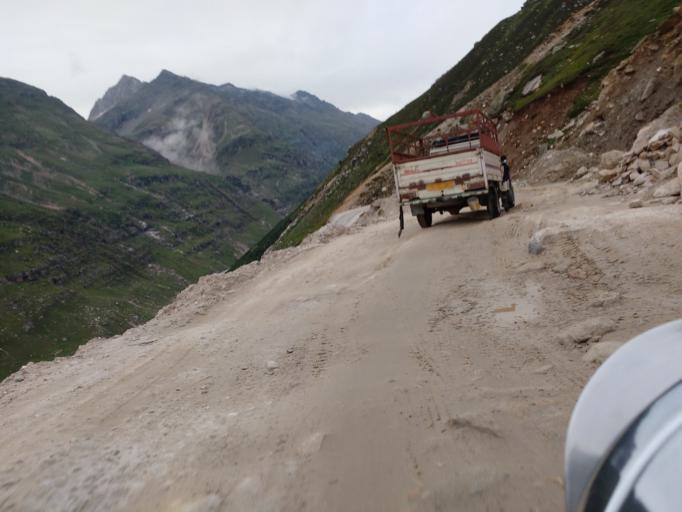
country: IN
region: Himachal Pradesh
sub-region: Kulu
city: Manali
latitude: 32.3786
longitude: 77.2677
